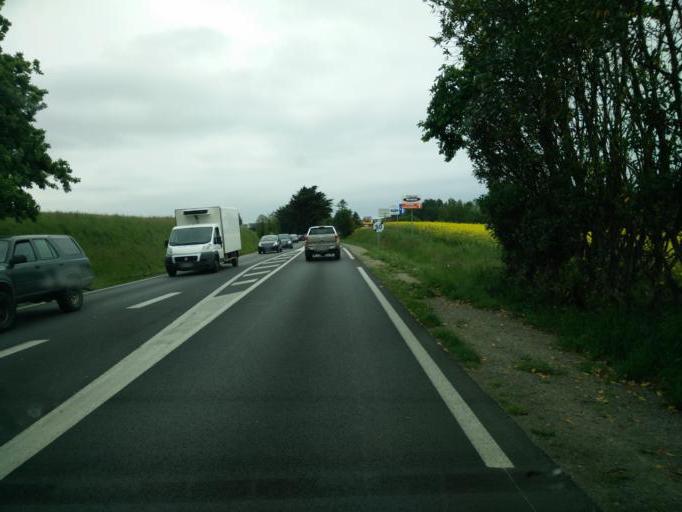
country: FR
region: Brittany
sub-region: Departement du Finistere
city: Concarneau
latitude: 47.8739
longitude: -3.8983
